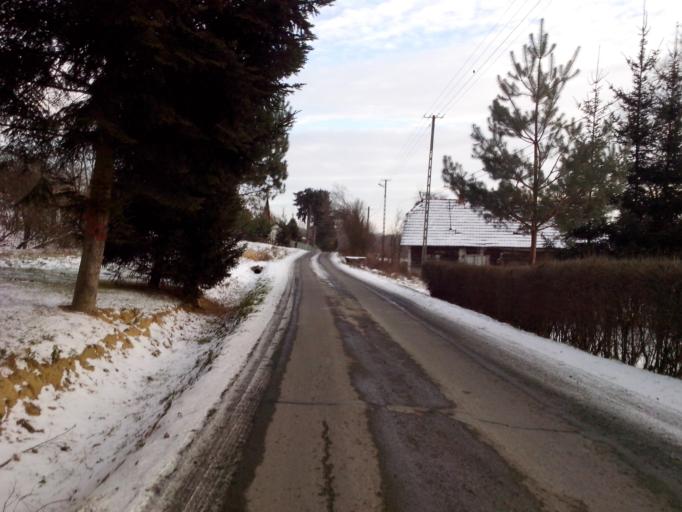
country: PL
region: Subcarpathian Voivodeship
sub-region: Powiat strzyzowski
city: Strzyzow
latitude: 49.8525
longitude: 21.8054
